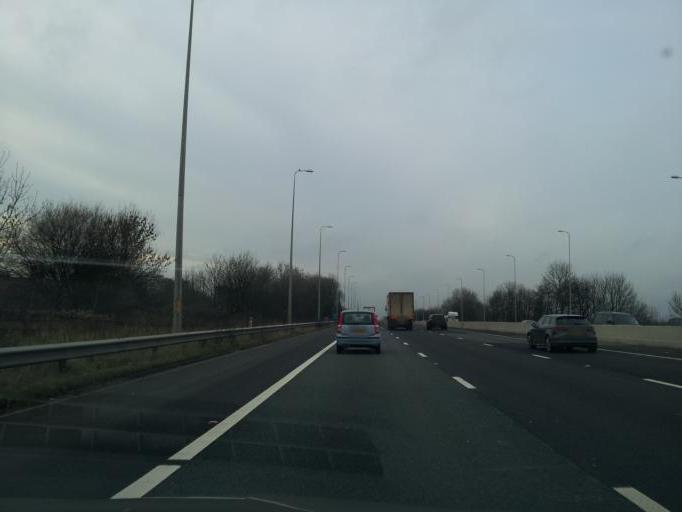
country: GB
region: England
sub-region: Borough of Rochdale
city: Milnrow
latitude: 53.5925
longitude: -2.1364
